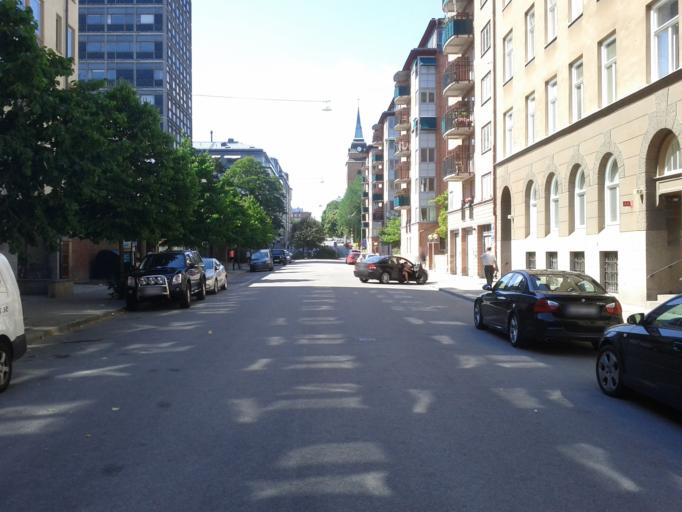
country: SE
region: Stockholm
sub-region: Solna Kommun
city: Solna
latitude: 59.3339
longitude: 18.0270
